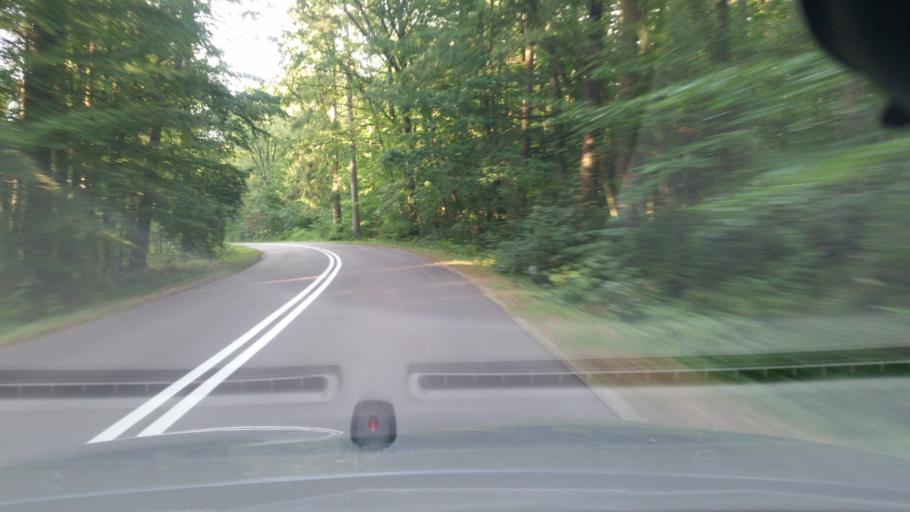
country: PL
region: Pomeranian Voivodeship
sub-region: Powiat wejherowski
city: Choczewo
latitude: 54.7478
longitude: 17.7455
